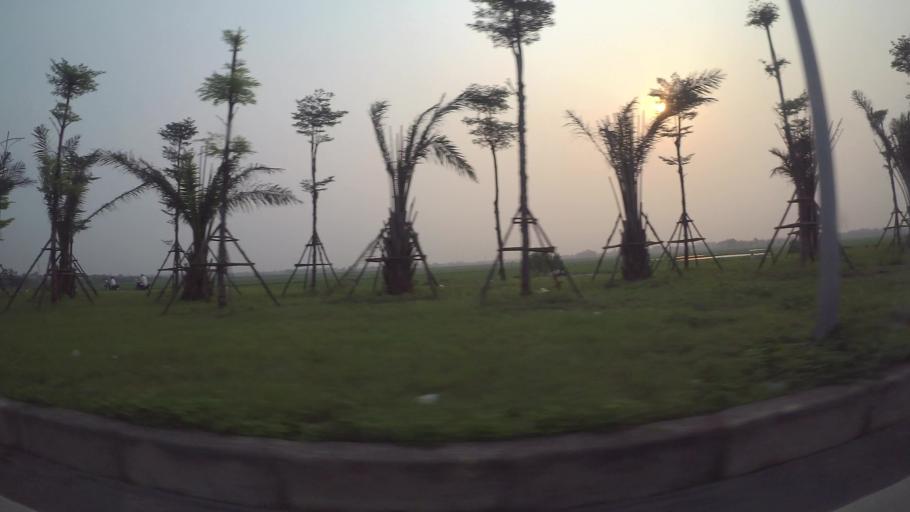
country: VN
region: Ha Noi
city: Kim Bai
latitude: 20.8794
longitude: 105.8002
